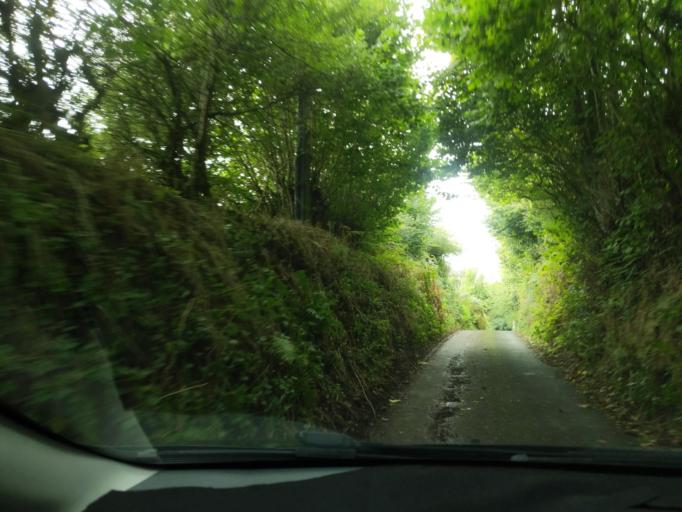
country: GB
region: England
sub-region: Cornwall
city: Lostwithiel
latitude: 50.3939
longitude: -4.7041
